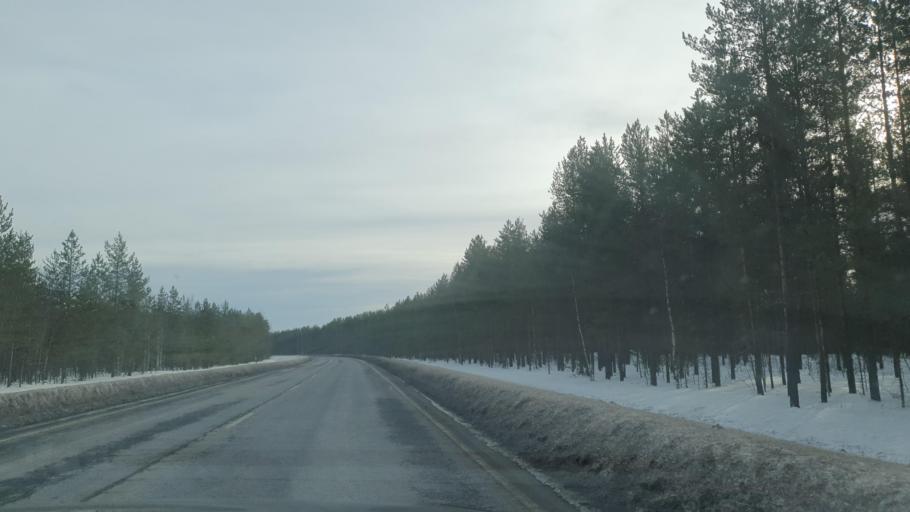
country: FI
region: Northern Ostrobothnia
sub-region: Oulunkaari
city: Utajaervi
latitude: 64.7097
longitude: 26.5161
